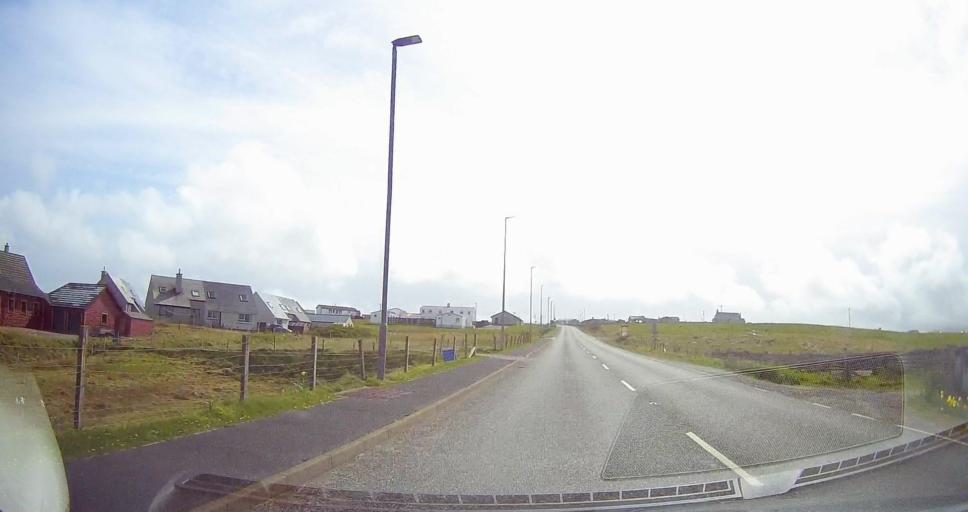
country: GB
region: Scotland
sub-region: Shetland Islands
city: Sandwick
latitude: 59.9243
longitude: -1.2982
